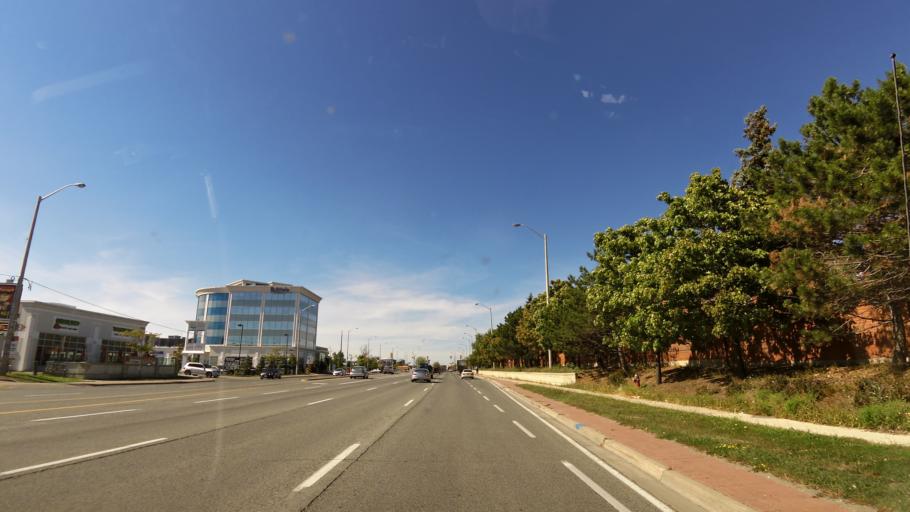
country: CA
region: Ontario
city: Brampton
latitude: 43.6637
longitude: -79.7298
